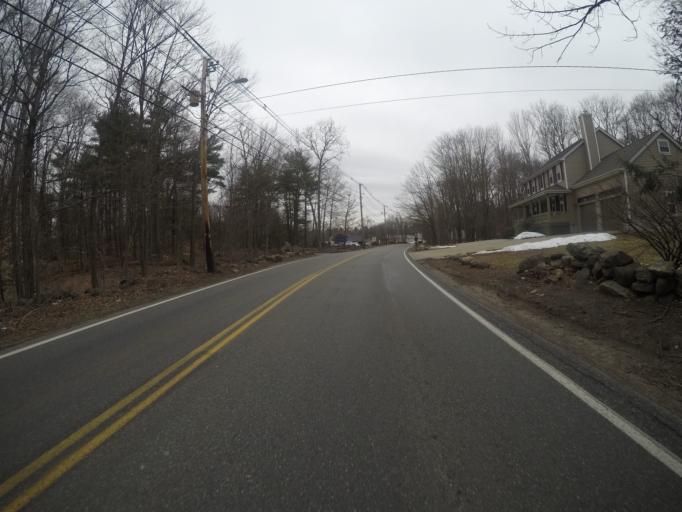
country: US
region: Massachusetts
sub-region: Bristol County
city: Easton
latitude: 42.0375
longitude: -71.0955
